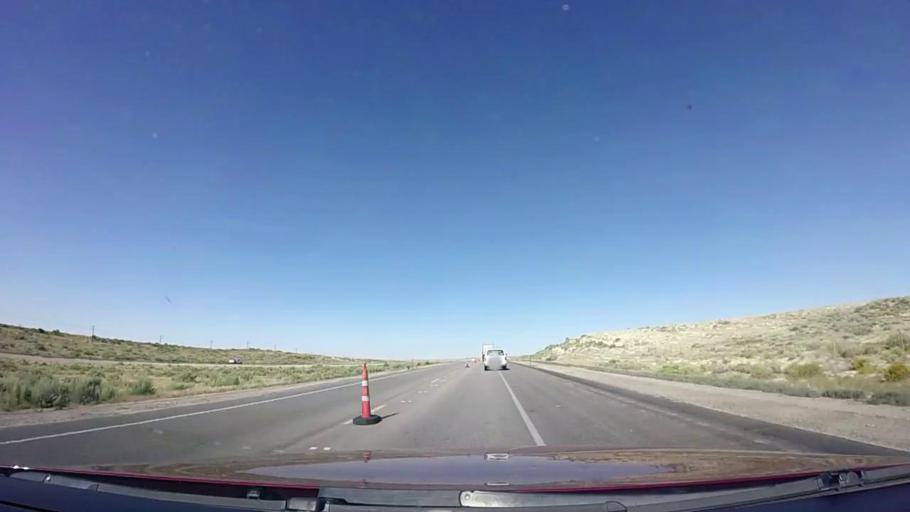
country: US
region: Wyoming
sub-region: Carbon County
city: Rawlins
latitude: 41.7065
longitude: -107.8655
